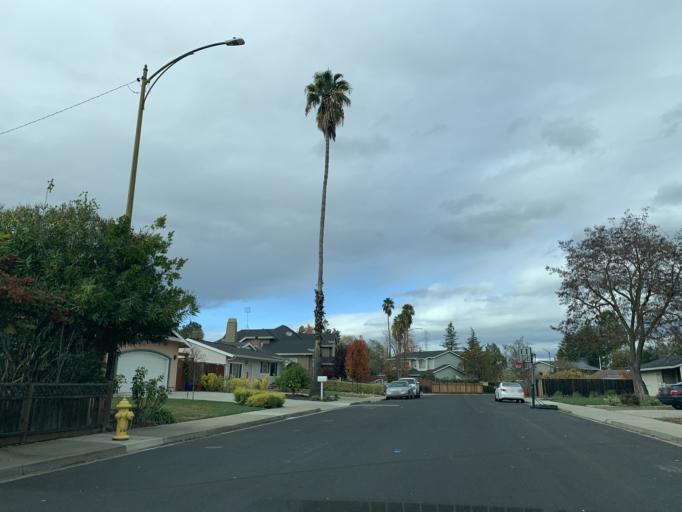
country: US
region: California
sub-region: Santa Clara County
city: Monte Sereno
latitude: 37.2610
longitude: -121.9805
